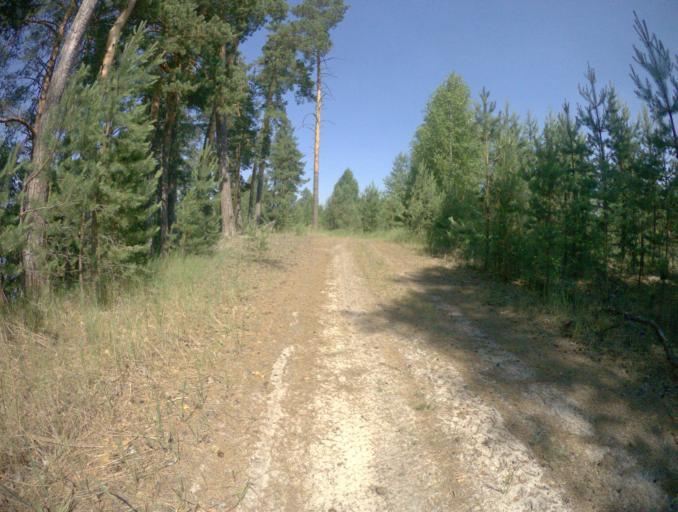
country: RU
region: Ivanovo
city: Talitsy
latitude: 56.3821
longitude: 42.2898
